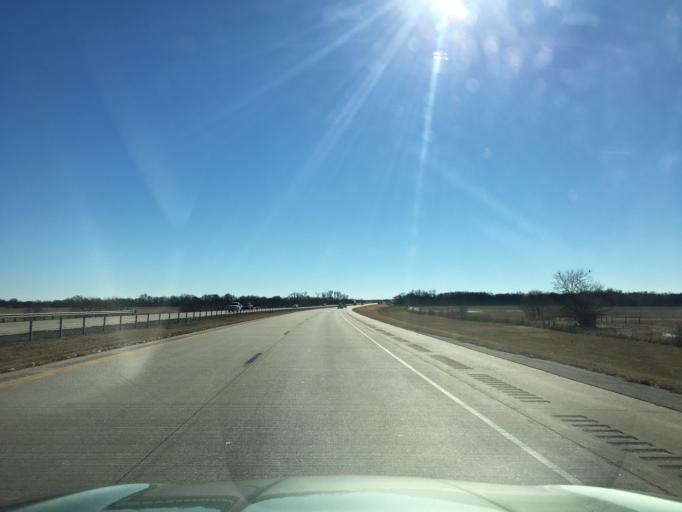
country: US
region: Oklahoma
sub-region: Kay County
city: Tonkawa
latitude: 36.4848
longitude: -97.3277
